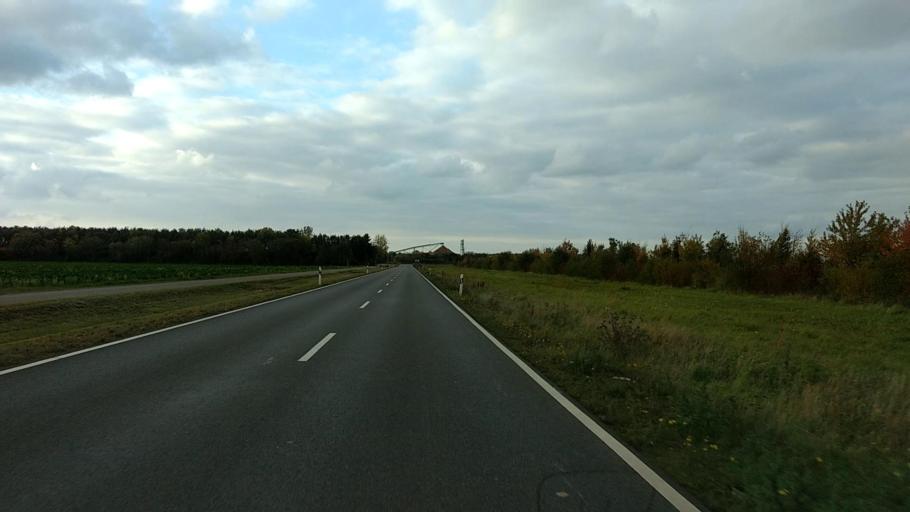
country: DE
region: North Rhine-Westphalia
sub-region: Regierungsbezirk Koln
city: Kerpen
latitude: 50.8714
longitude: 6.6427
